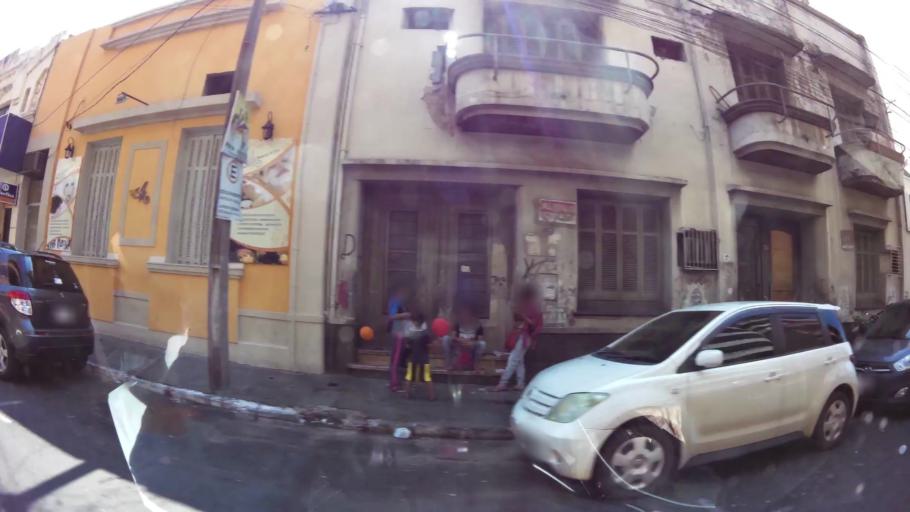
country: PY
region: Asuncion
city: Asuncion
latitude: -25.2822
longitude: -57.6388
